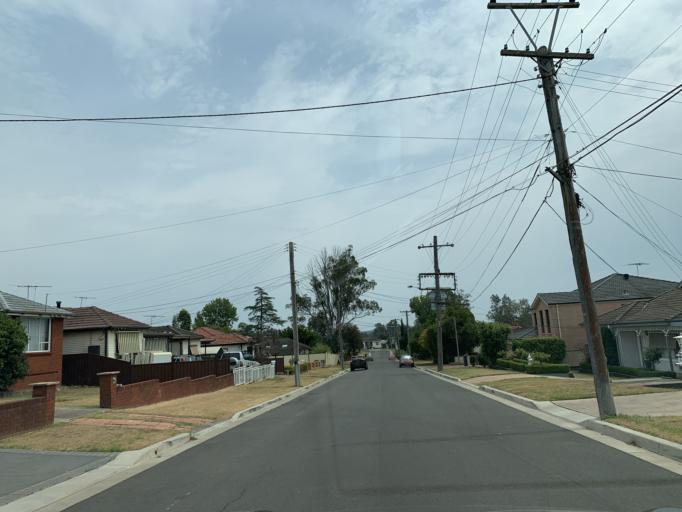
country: AU
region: New South Wales
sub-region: Blacktown
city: Blacktown
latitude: -33.7818
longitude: 150.8968
